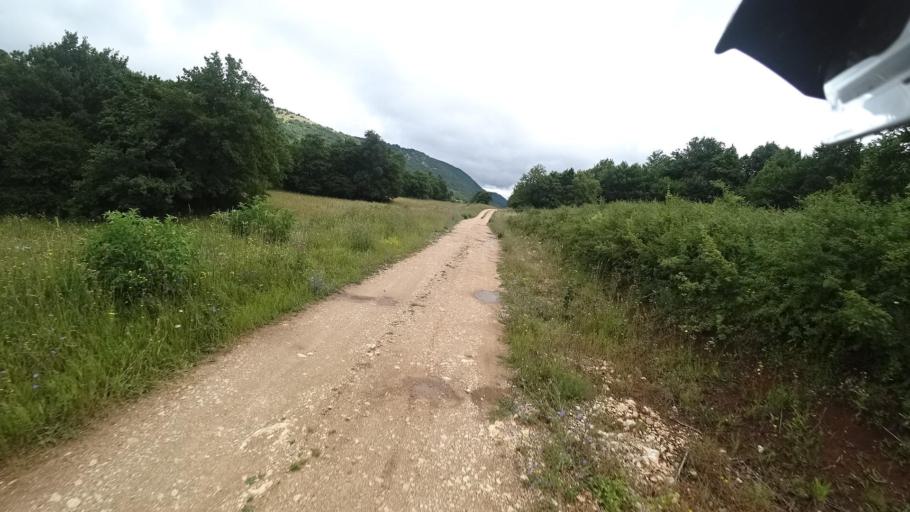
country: HR
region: Licko-Senjska
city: Jezerce
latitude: 44.7154
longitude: 15.5165
